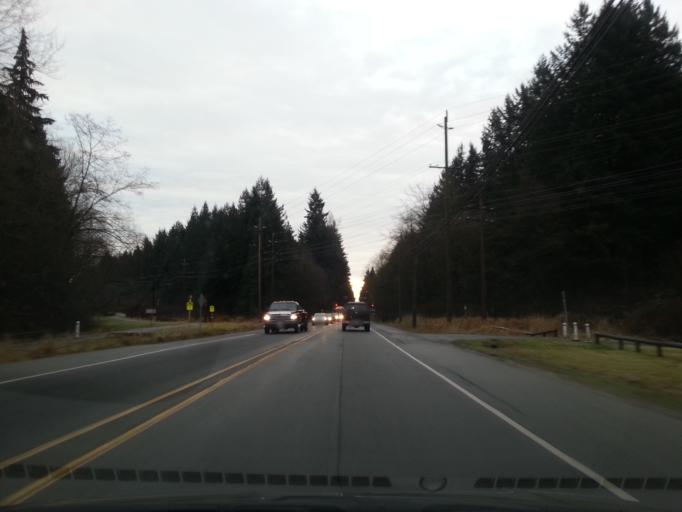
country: CA
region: British Columbia
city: Surrey
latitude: 49.1757
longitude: -122.8263
